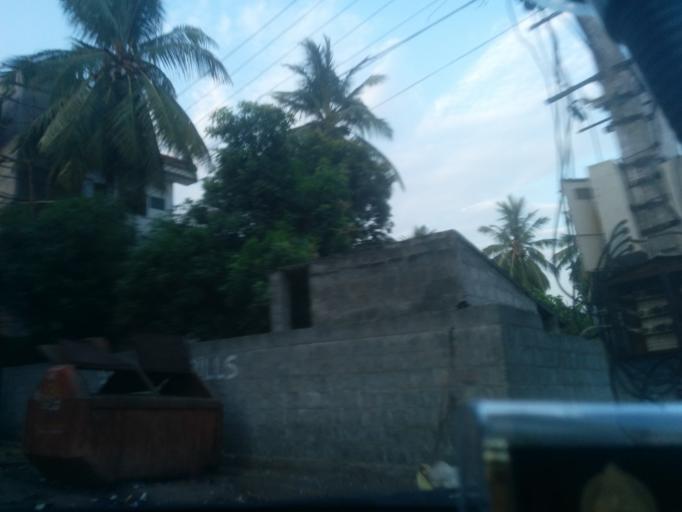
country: IN
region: Andhra Pradesh
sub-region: East Godavari
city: Rajahmundry
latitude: 17.0074
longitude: 81.7967
